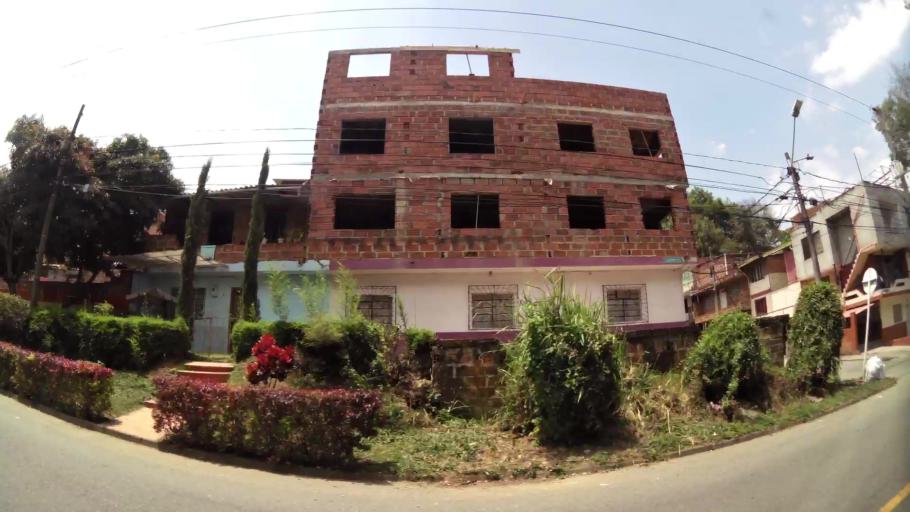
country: CO
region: Antioquia
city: Bello
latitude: 6.3026
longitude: -75.5690
